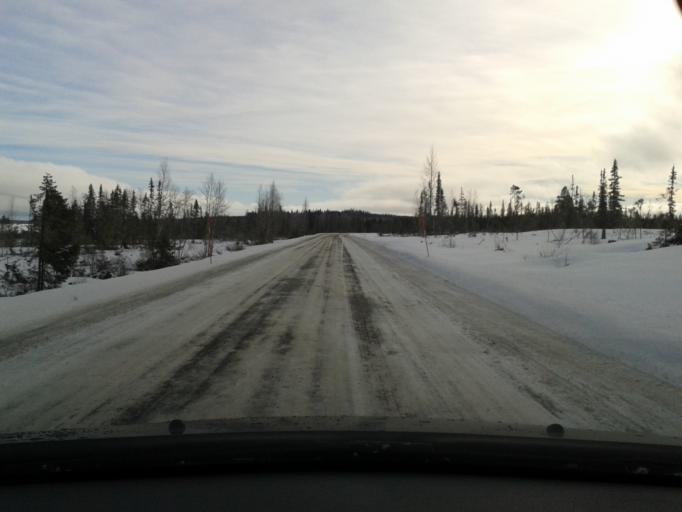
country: SE
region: Vaesterbotten
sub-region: Vilhelmina Kommun
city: Sjoberg
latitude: 64.7512
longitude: 16.1685
